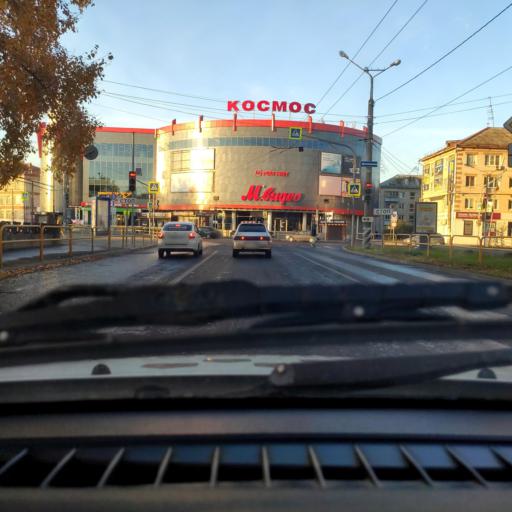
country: RU
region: Samara
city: Tol'yatti
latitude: 53.5108
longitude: 49.4159
